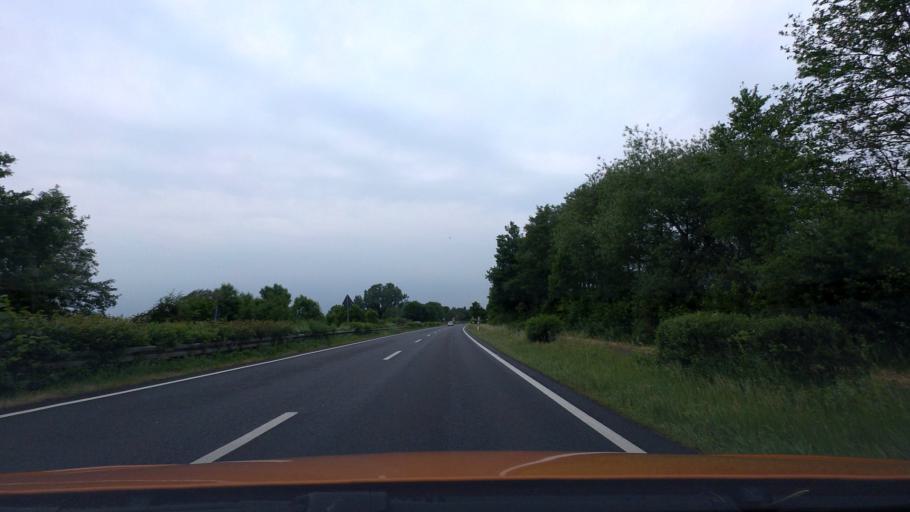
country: DE
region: Lower Saxony
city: Neustadt am Rubenberge
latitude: 52.4984
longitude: 9.4772
